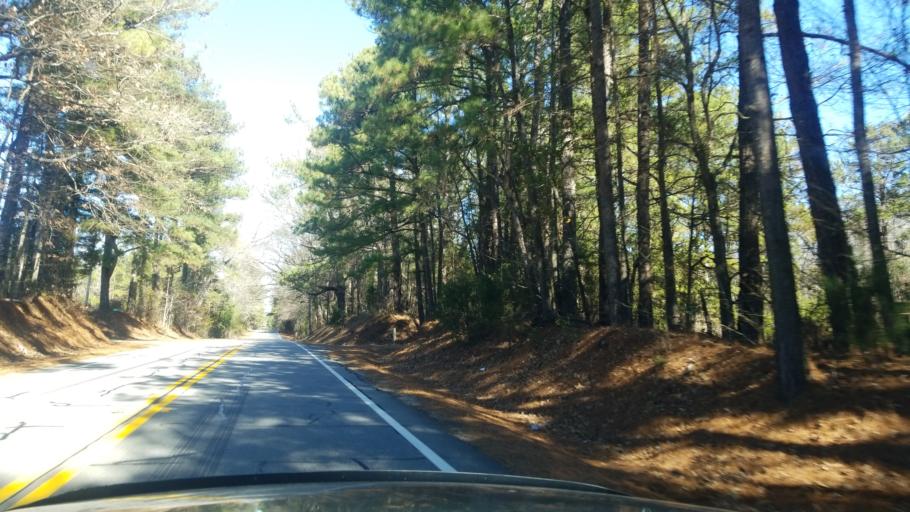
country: US
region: Georgia
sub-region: Harris County
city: Hamilton
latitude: 32.6791
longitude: -84.8587
